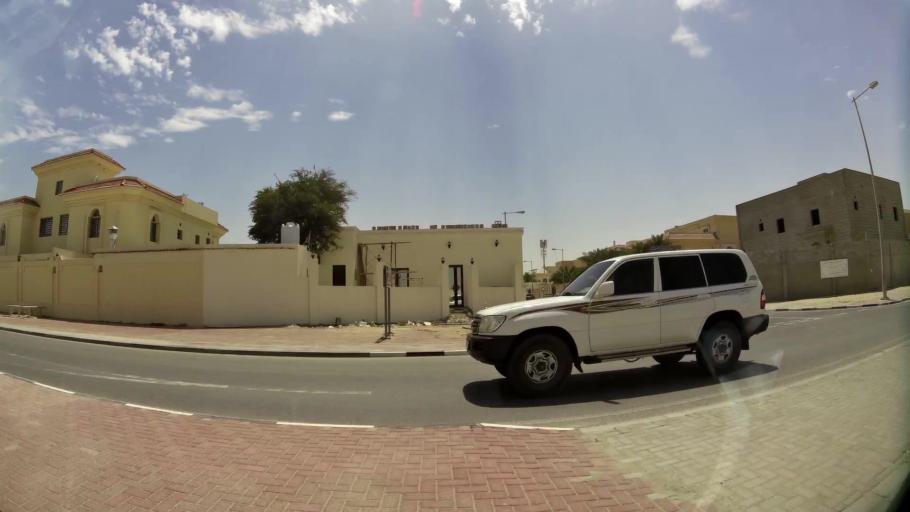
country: QA
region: Baladiyat ar Rayyan
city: Ar Rayyan
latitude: 25.2998
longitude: 51.4172
